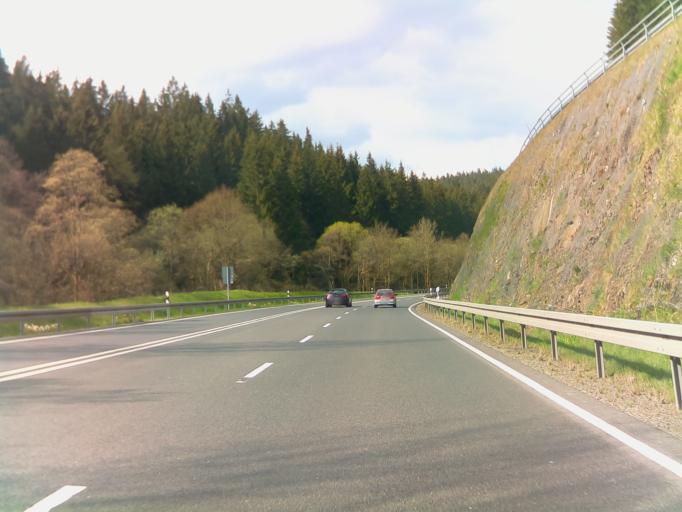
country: DE
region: Bavaria
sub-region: Upper Franconia
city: Teuschnitz
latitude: 50.4082
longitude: 11.3529
